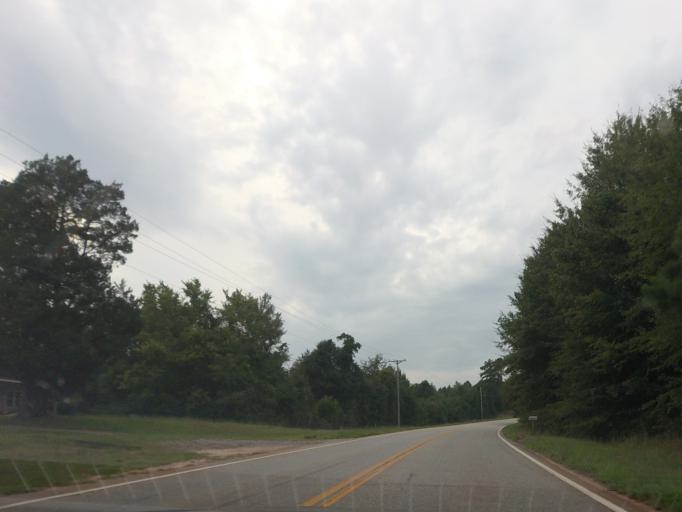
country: US
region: Georgia
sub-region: Twiggs County
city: Jeffersonville
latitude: 32.7378
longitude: -83.4252
